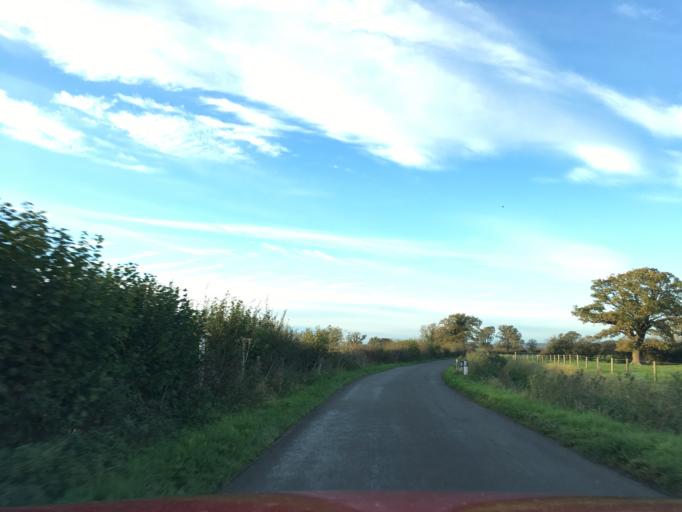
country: GB
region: England
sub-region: South Gloucestershire
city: Hill
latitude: 51.6404
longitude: -2.5066
